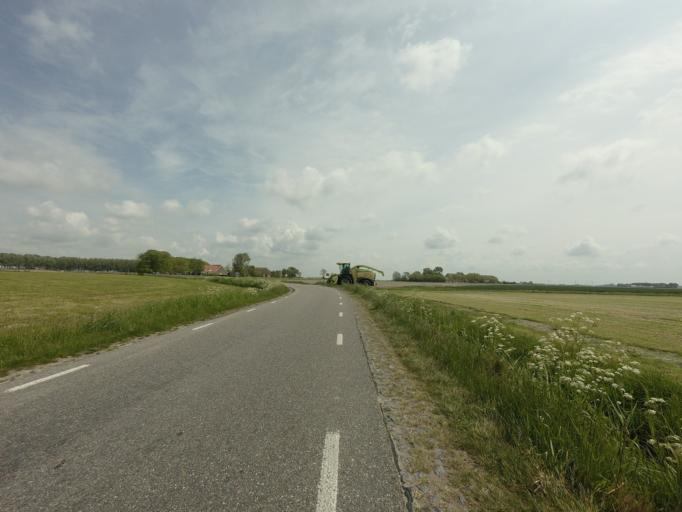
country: NL
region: Friesland
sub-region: Sudwest Fryslan
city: Bolsward
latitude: 53.1114
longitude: 5.4857
